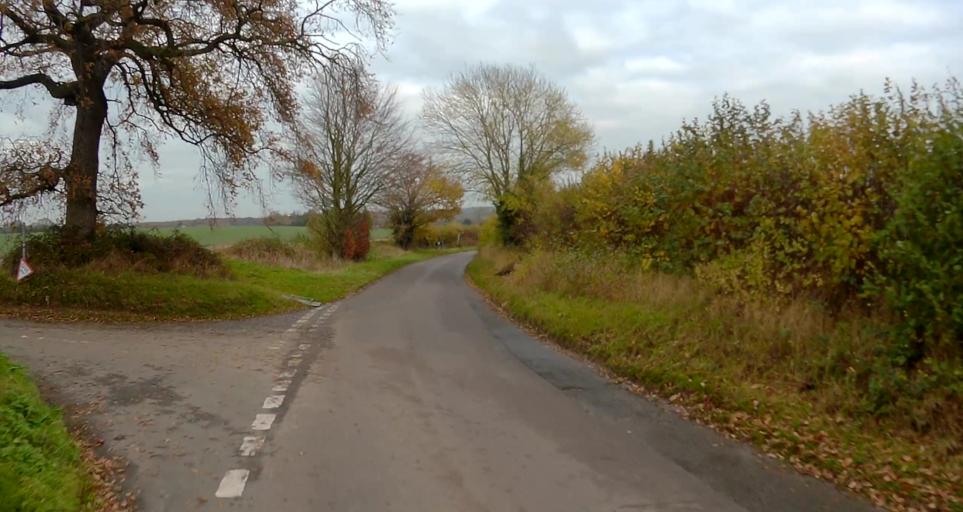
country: GB
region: England
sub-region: Hampshire
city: Long Sutton
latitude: 51.2280
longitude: -0.8751
